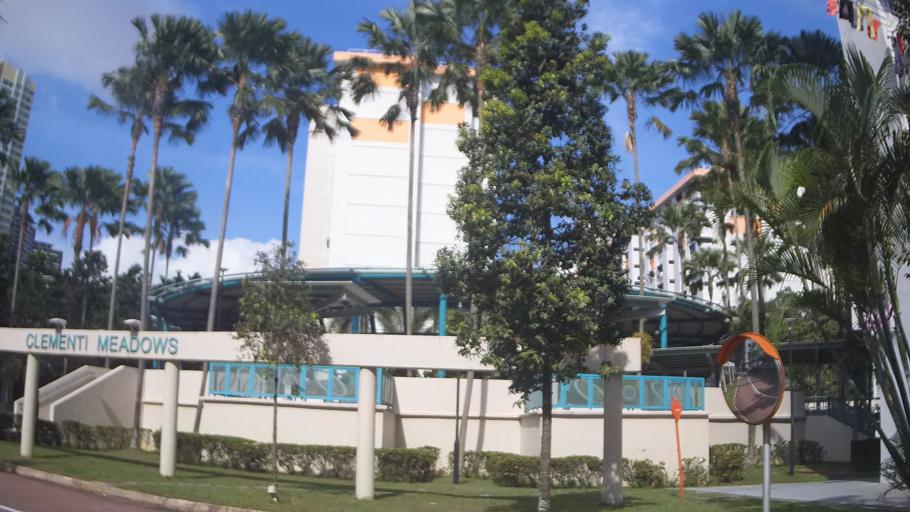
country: SG
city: Singapore
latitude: 1.3209
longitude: 103.7660
